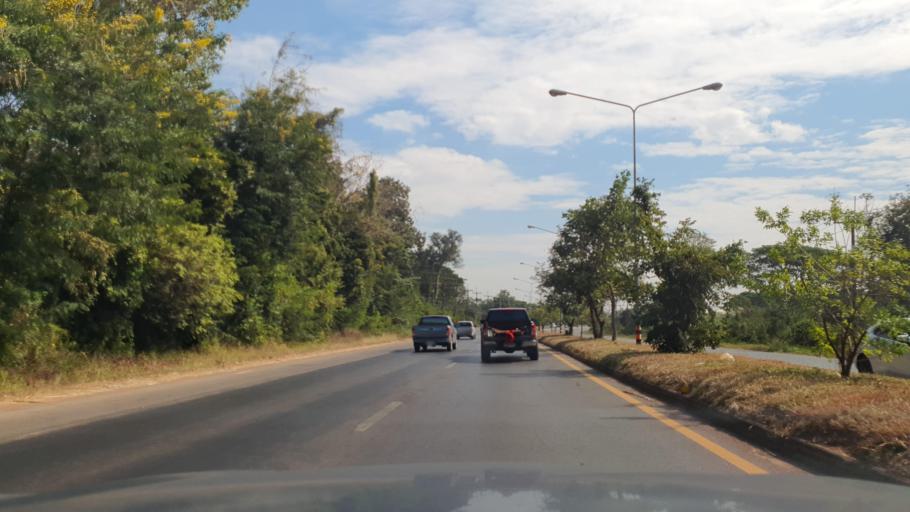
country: TH
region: Kalasin
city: Yang Talat
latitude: 16.4057
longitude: 103.4240
